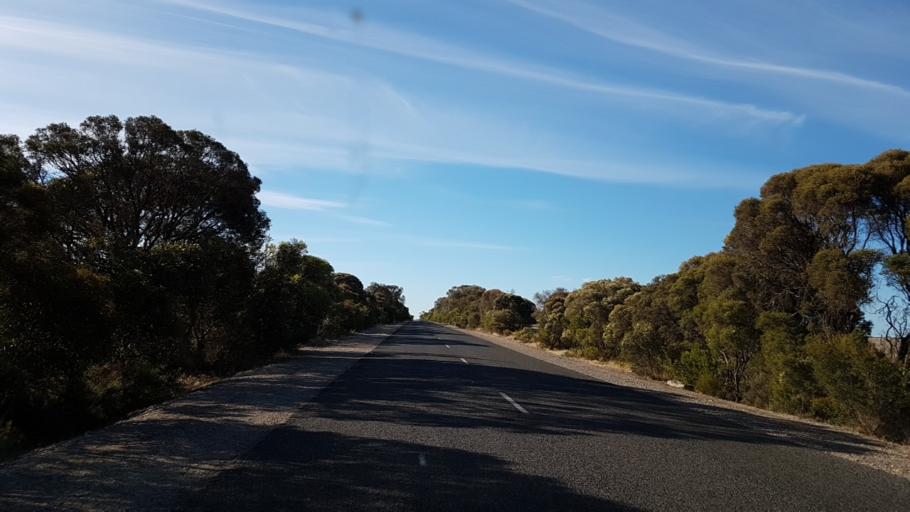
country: AU
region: South Australia
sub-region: Yorke Peninsula
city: Honiton
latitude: -34.9584
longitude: 137.1038
